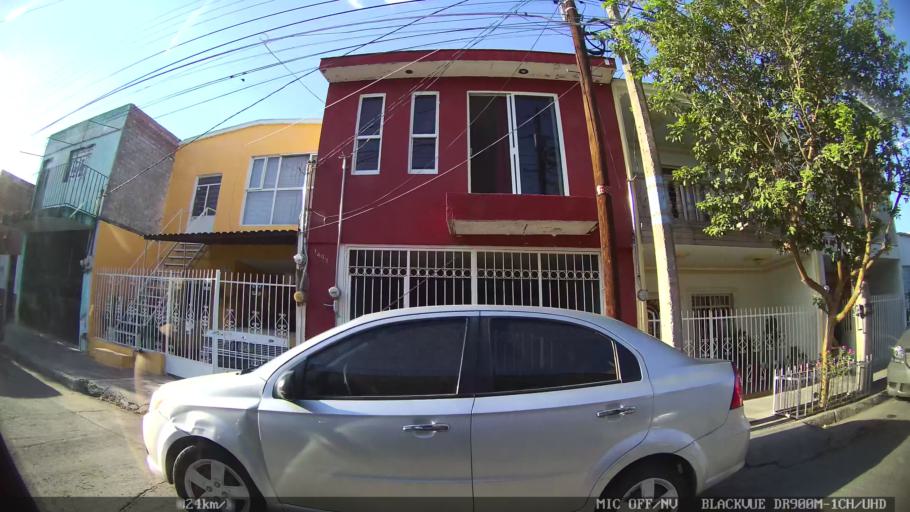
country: MX
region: Jalisco
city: Tlaquepaque
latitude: 20.6989
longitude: -103.2998
